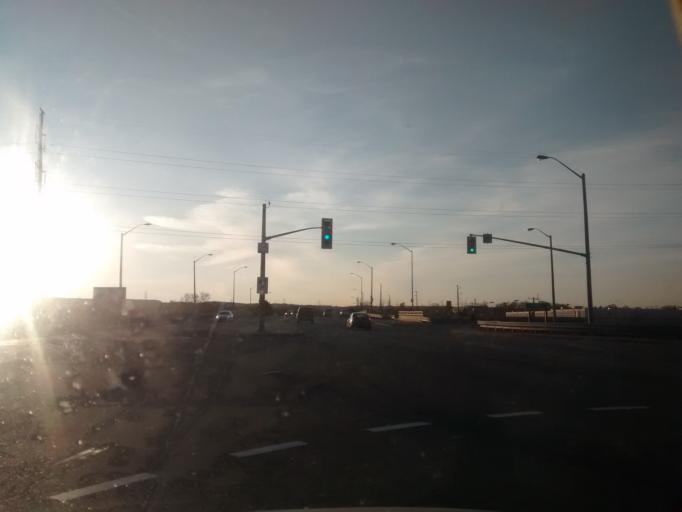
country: CA
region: Ontario
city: Burlington
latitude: 43.3530
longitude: -79.8053
